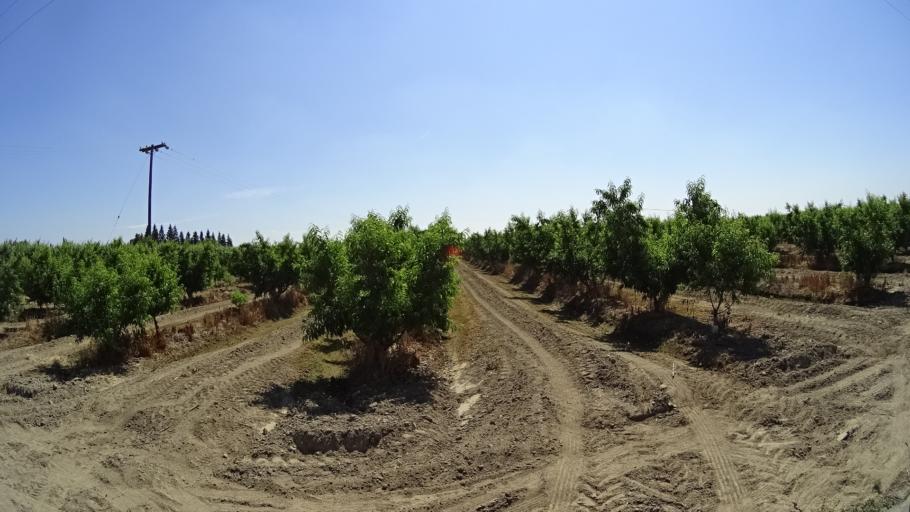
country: US
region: California
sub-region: Fresno County
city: Kingsburg
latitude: 36.4577
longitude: -119.5914
